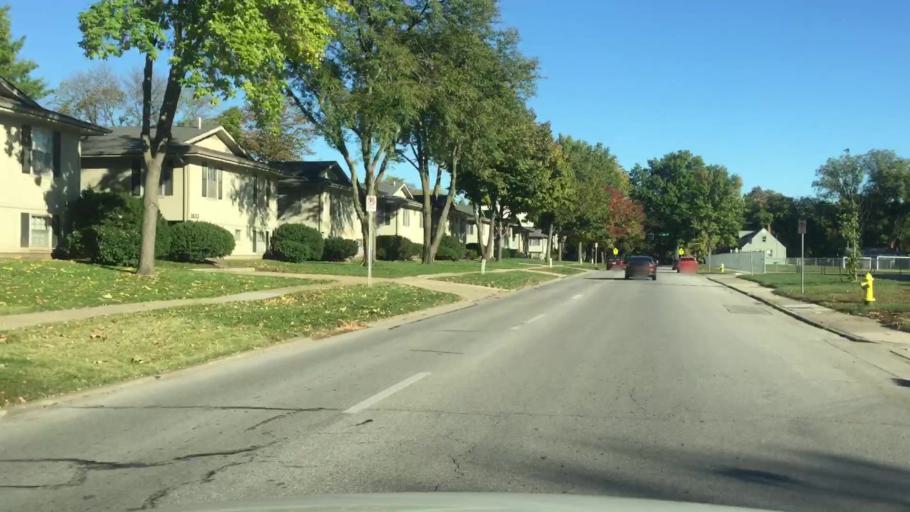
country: US
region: Kansas
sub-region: Douglas County
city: Lawrence
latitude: 38.9504
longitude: -95.2382
